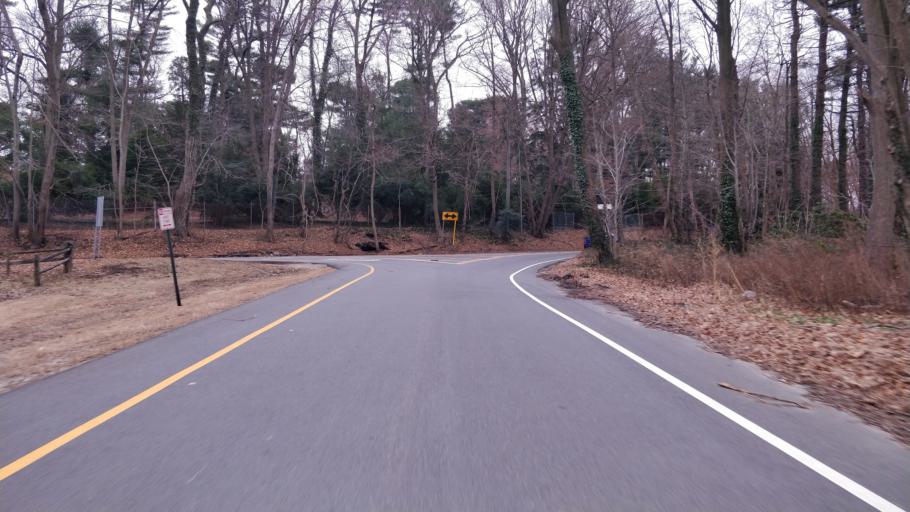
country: US
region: New York
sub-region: Nassau County
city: Old Westbury
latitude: 40.7812
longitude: -73.5907
